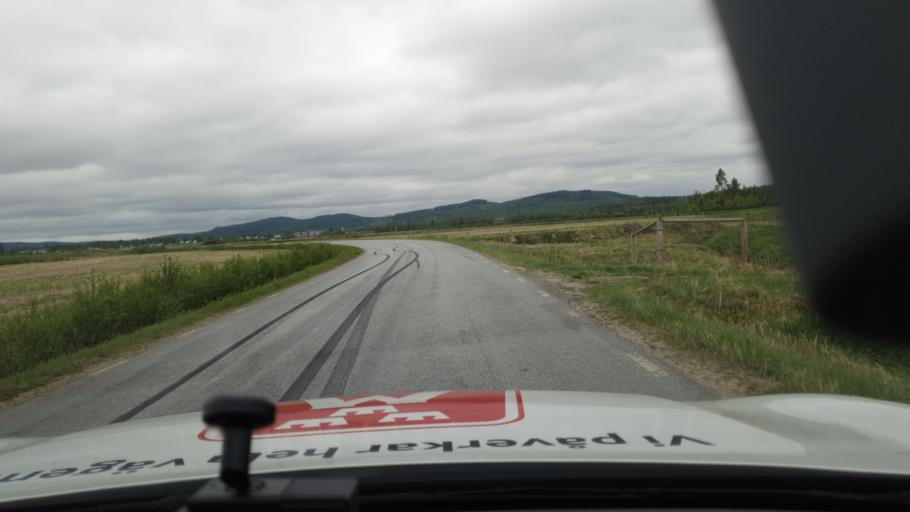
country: SE
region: Vaesterbotten
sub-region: Vannas Kommun
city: Vannasby
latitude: 63.9347
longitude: 19.8344
